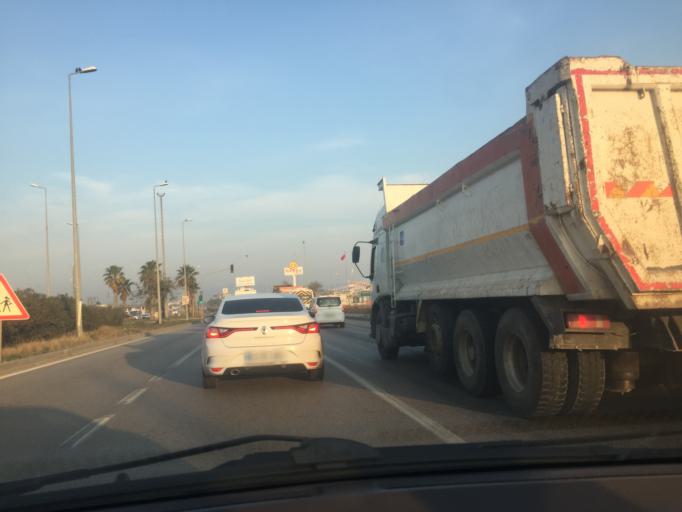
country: TR
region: Balikesir
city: Bandirma
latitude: 40.3232
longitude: 28.0045
